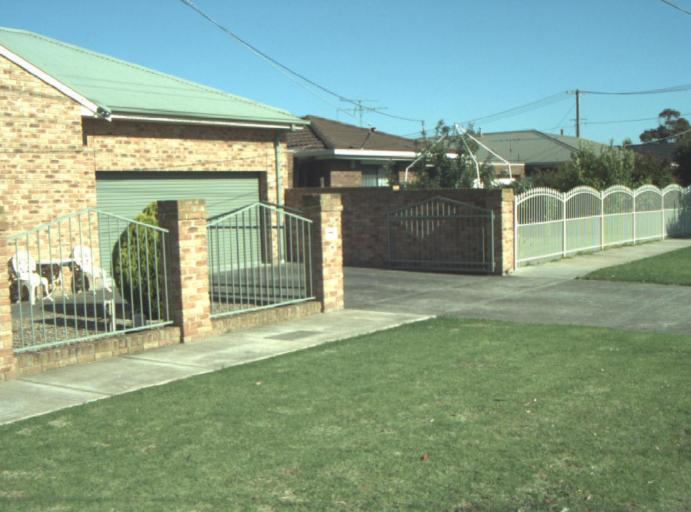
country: AU
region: Victoria
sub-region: Greater Geelong
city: Hamlyn Heights
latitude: -38.1135
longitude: 144.3227
